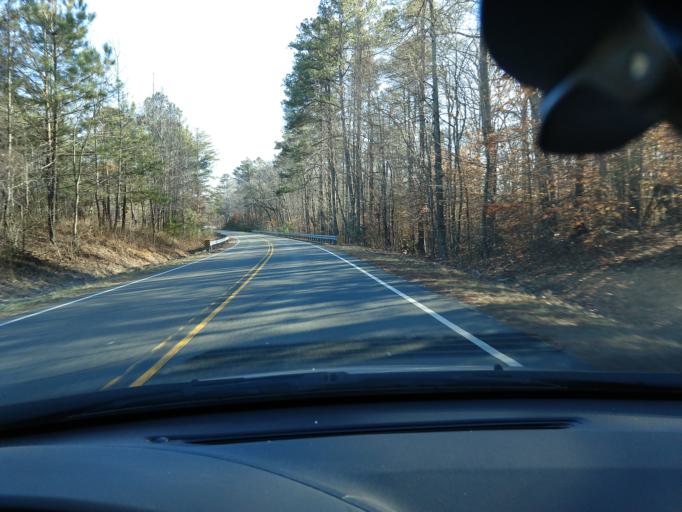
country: US
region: Virginia
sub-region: Charles City County
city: Charles City
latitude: 37.3140
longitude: -76.9672
